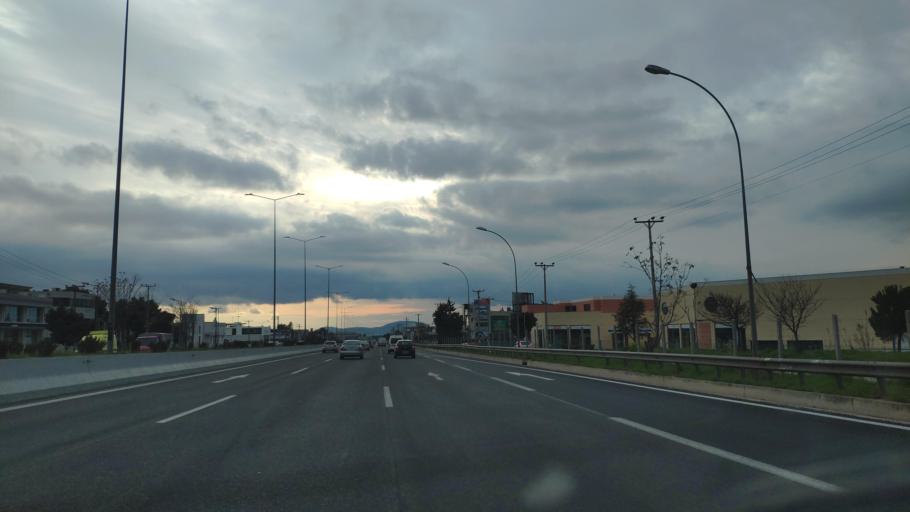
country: GR
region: Attica
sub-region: Nomarchia Athinas
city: Nea Erythraia
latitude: 38.1026
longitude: 23.8091
